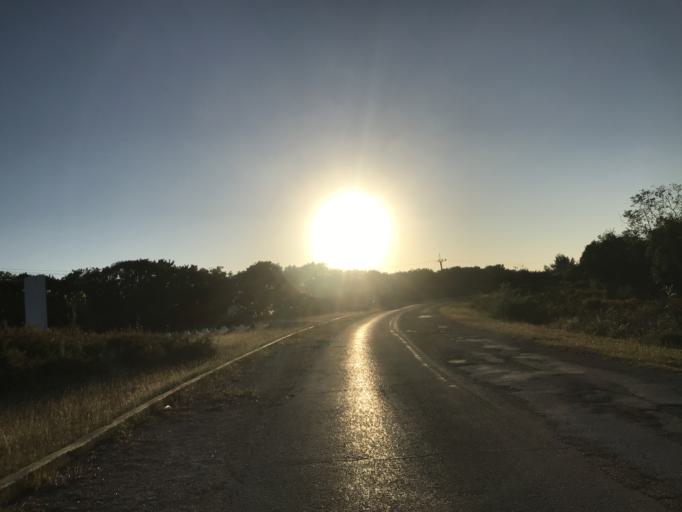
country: CU
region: Cienfuegos
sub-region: Municipio de Aguada de Pasajeros
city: Aguada de Pasajeros
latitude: 22.0670
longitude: -81.0416
